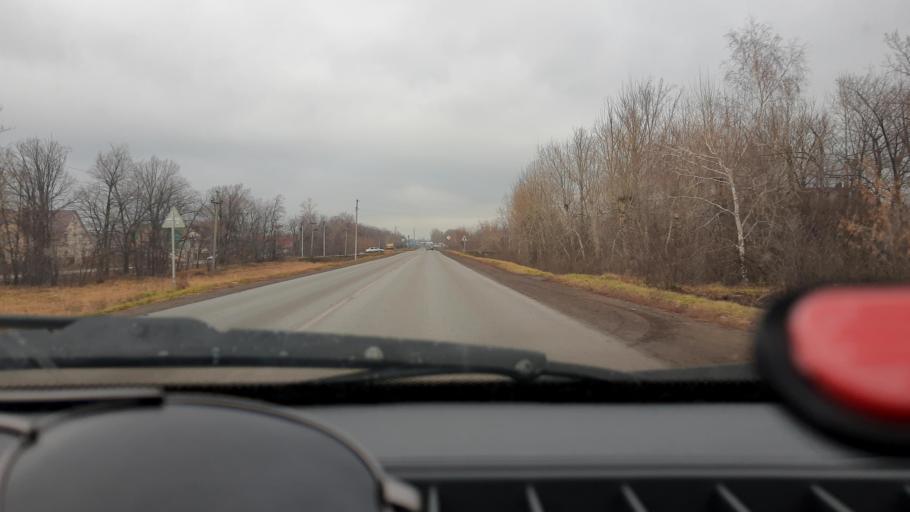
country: RU
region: Bashkortostan
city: Ufa
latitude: 54.6235
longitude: 55.9107
